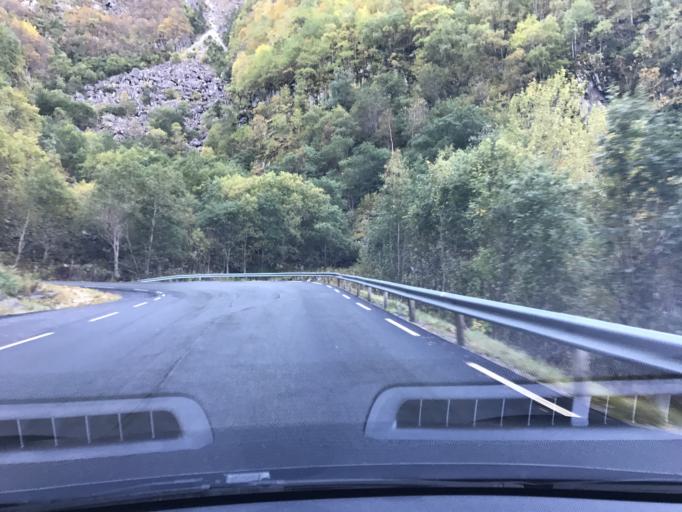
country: NO
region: Sogn og Fjordane
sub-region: Aurland
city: Aurlandsvangen
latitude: 60.8607
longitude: 7.3038
